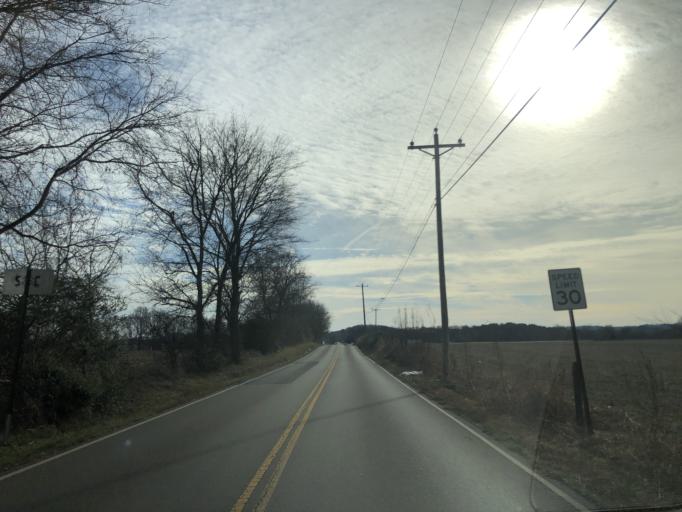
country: US
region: Tennessee
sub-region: Williamson County
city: Franklin
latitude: 35.9469
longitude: -86.9026
